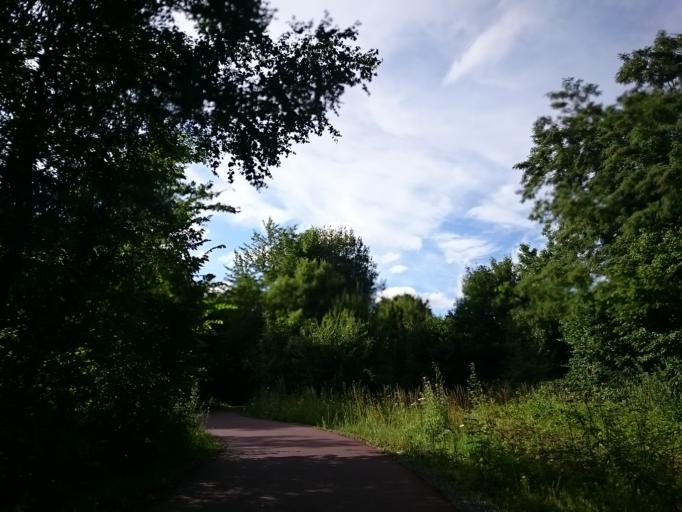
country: FR
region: Lower Normandy
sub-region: Departement du Calvados
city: Saint-Andre-sur-Orne
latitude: 49.1131
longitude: -0.3882
